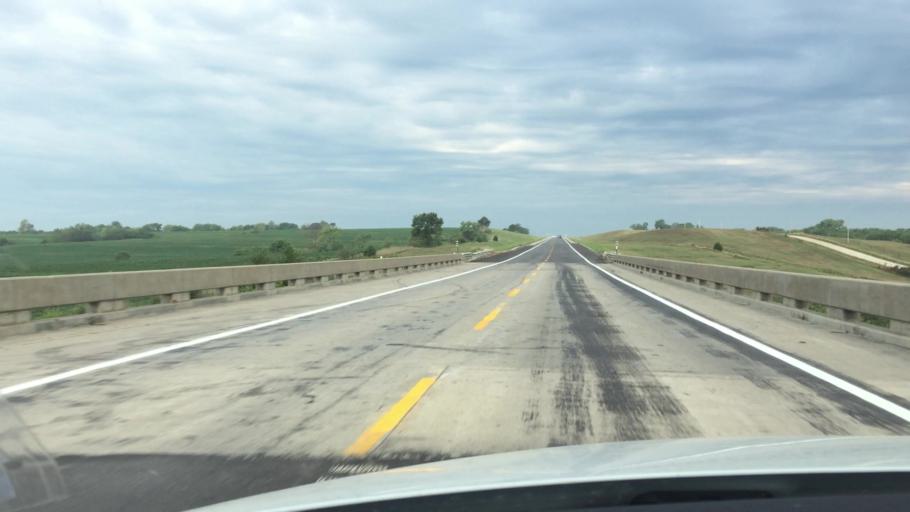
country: US
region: Kansas
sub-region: Doniphan County
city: Highland
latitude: 39.8412
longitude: -95.3775
